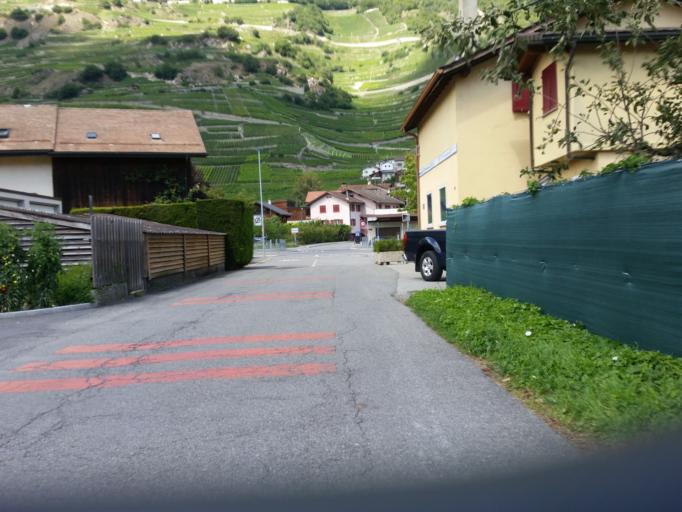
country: CH
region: Valais
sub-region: Martigny District
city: Fully
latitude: 46.1432
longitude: 7.1257
